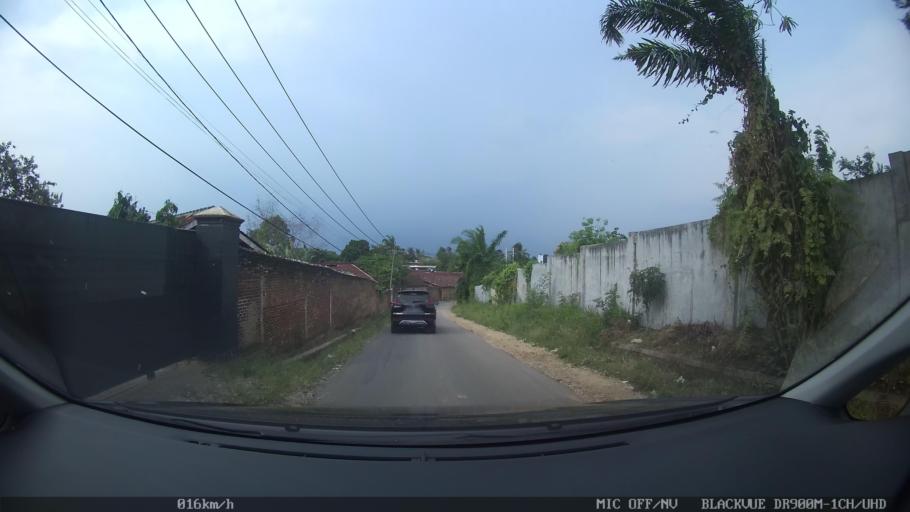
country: ID
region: Lampung
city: Kedaton
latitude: -5.3534
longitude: 105.2234
